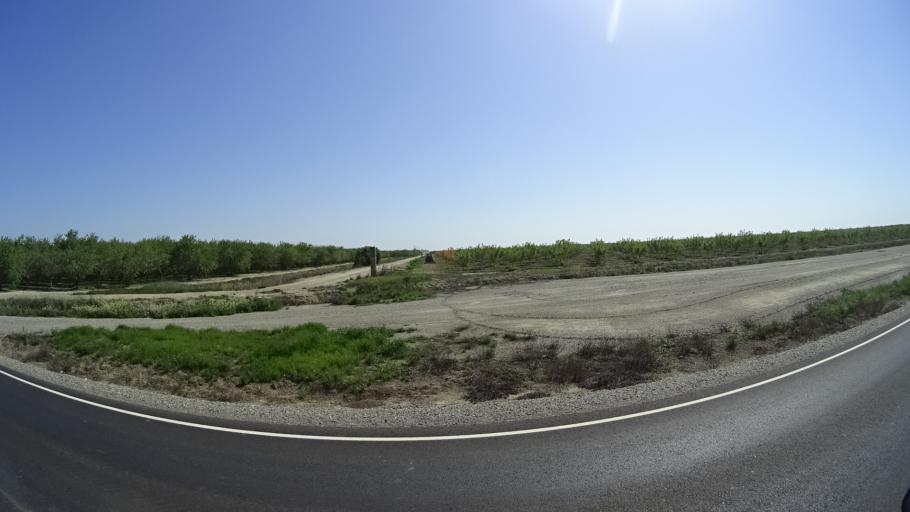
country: US
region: California
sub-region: Glenn County
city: Hamilton City
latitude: 39.6469
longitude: -122.0650
